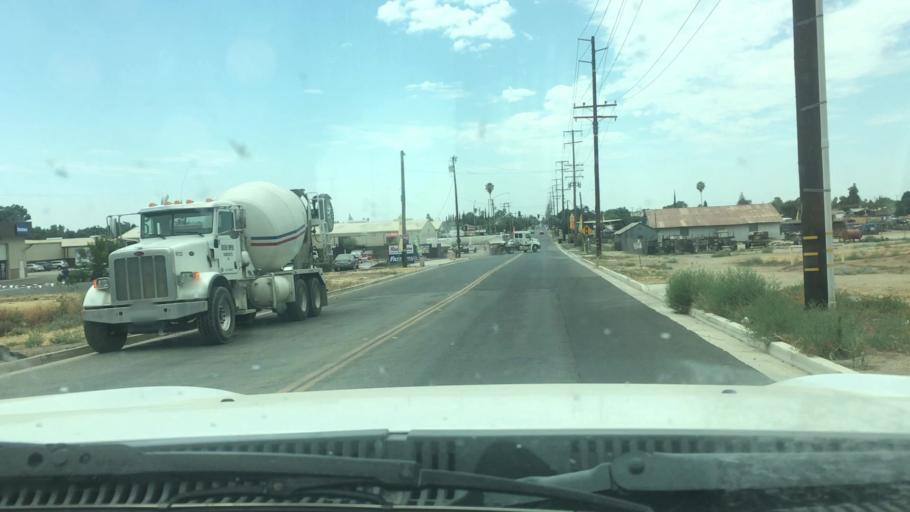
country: US
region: California
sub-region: Tulare County
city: Porterville
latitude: 36.0982
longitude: -119.0374
